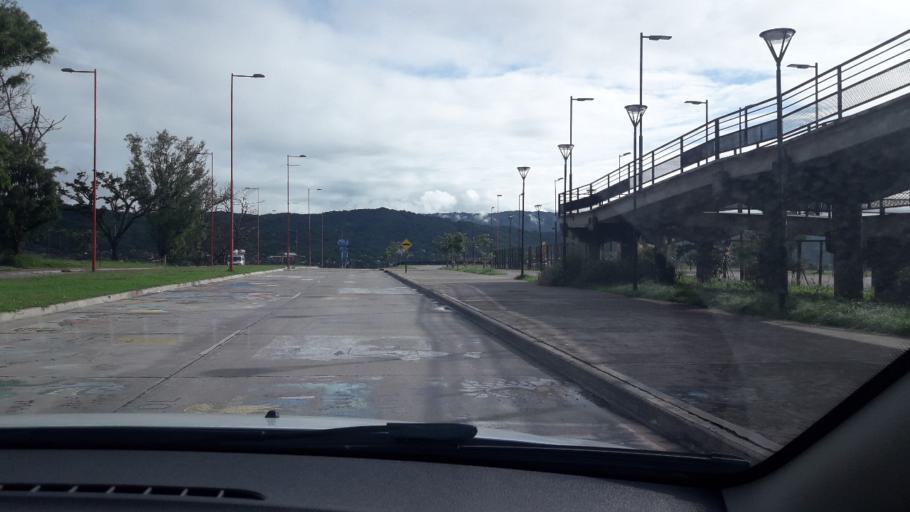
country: AR
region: Jujuy
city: San Salvador de Jujuy
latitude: -24.1817
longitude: -65.3303
